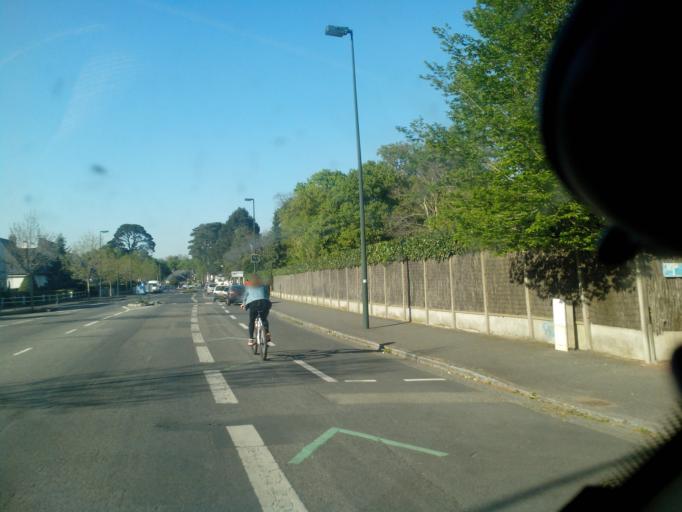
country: FR
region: Pays de la Loire
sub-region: Departement de la Loire-Atlantique
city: Orvault
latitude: 47.2517
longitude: -1.5981
